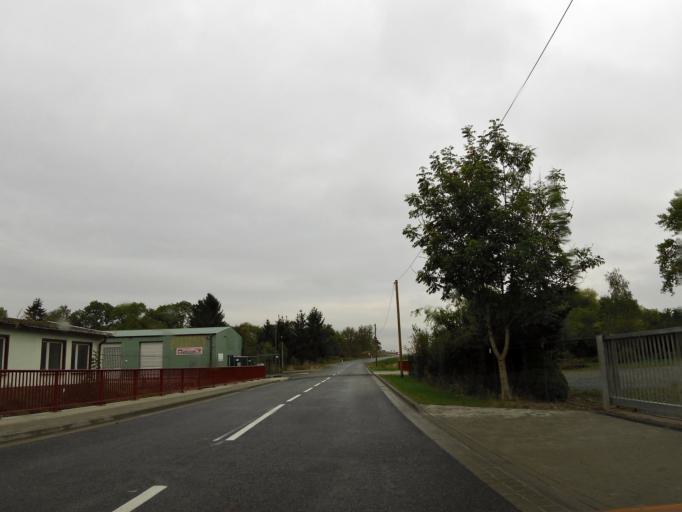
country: DE
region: Saxony-Anhalt
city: Ballenstedt
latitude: 51.7260
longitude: 11.2497
